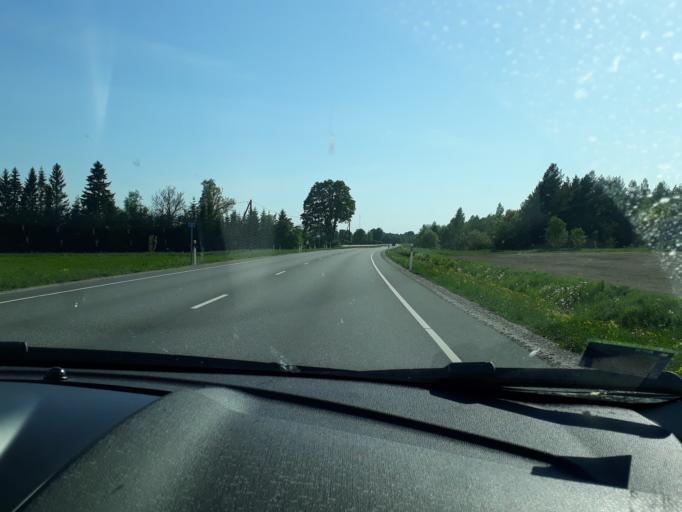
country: EE
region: Paernumaa
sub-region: Tootsi vald
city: Tootsi
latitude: 58.5590
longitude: 24.8649
